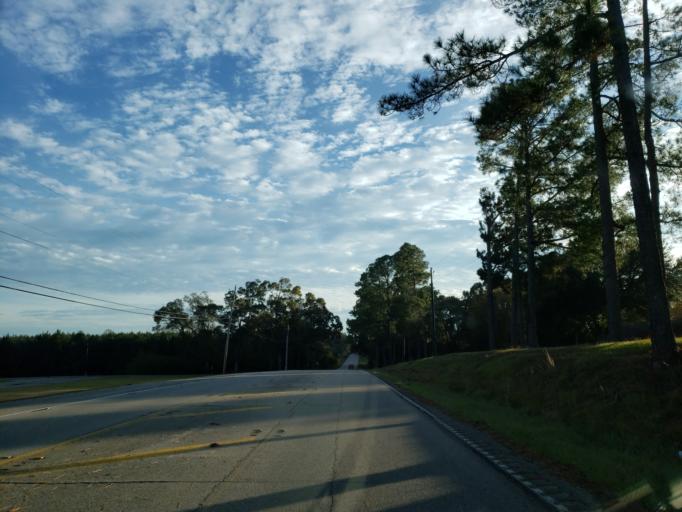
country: US
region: Mississippi
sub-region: Lamar County
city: Purvis
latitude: 31.1321
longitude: -89.4061
